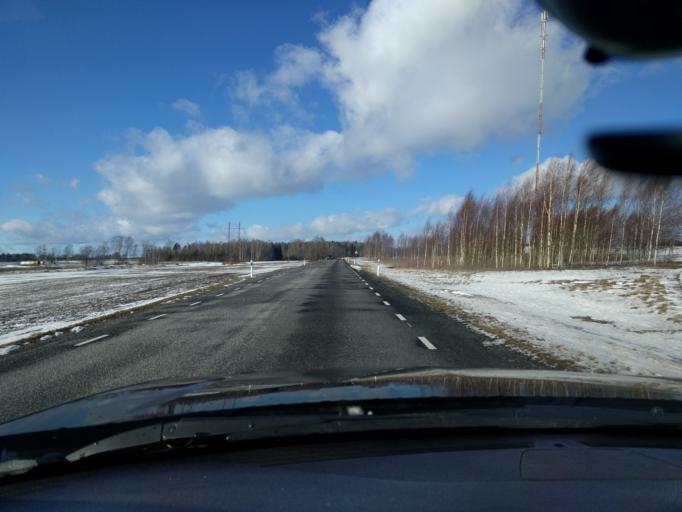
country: EE
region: Harju
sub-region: Anija vald
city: Kehra
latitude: 59.2520
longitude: 25.3347
